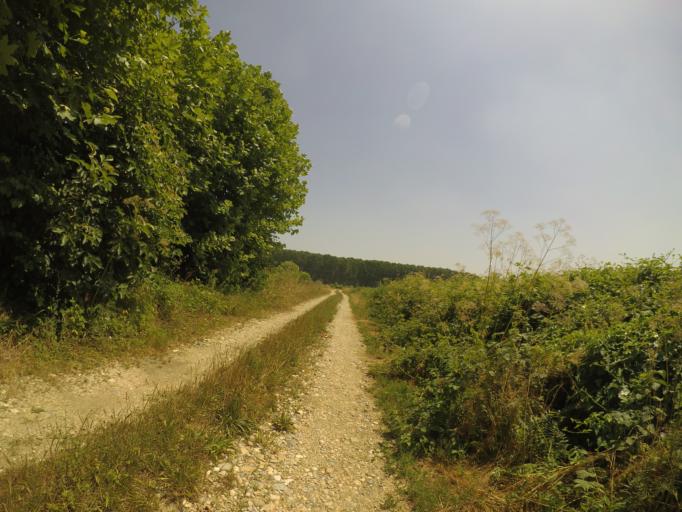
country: IT
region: Friuli Venezia Giulia
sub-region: Provincia di Udine
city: Bertiolo
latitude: 45.9297
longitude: 13.0478
